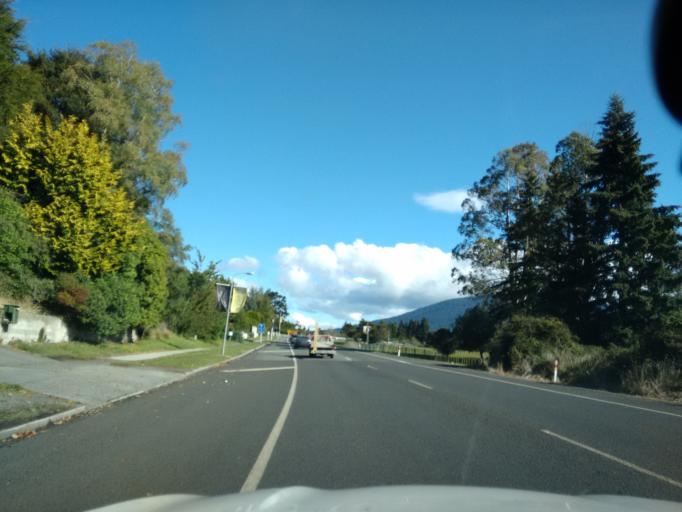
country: NZ
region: Waikato
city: Turangi
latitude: -38.9838
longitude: 175.8201
